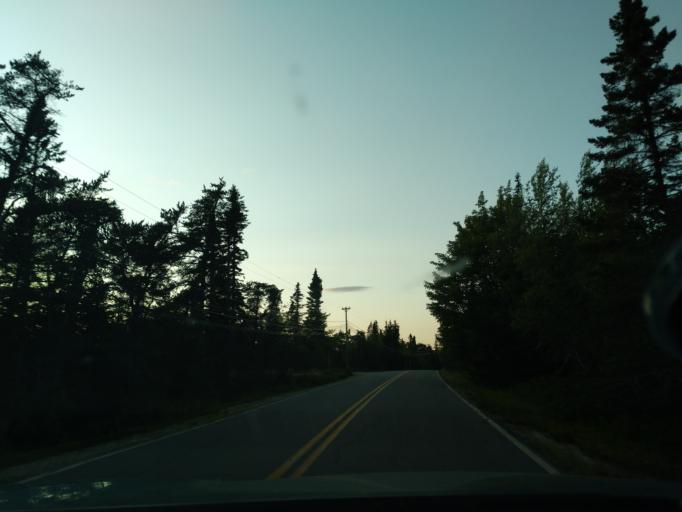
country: US
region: Maine
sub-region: Hancock County
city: Gouldsboro
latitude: 44.3777
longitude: -68.0361
